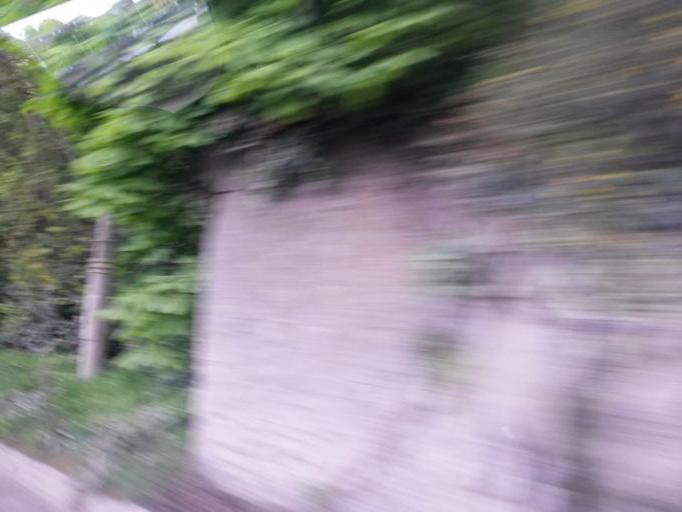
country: IE
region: Leinster
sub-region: Loch Garman
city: Enniscorthy
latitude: 52.4997
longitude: -6.5639
